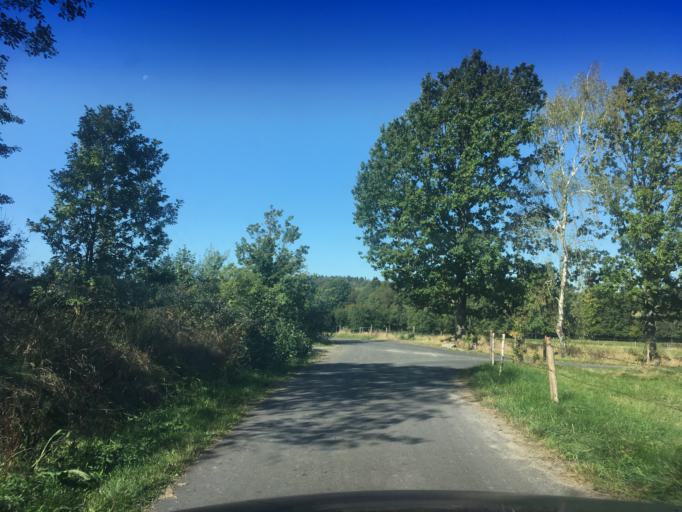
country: PL
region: Lower Silesian Voivodeship
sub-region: Powiat lubanski
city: Lesna
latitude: 51.0001
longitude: 15.1924
